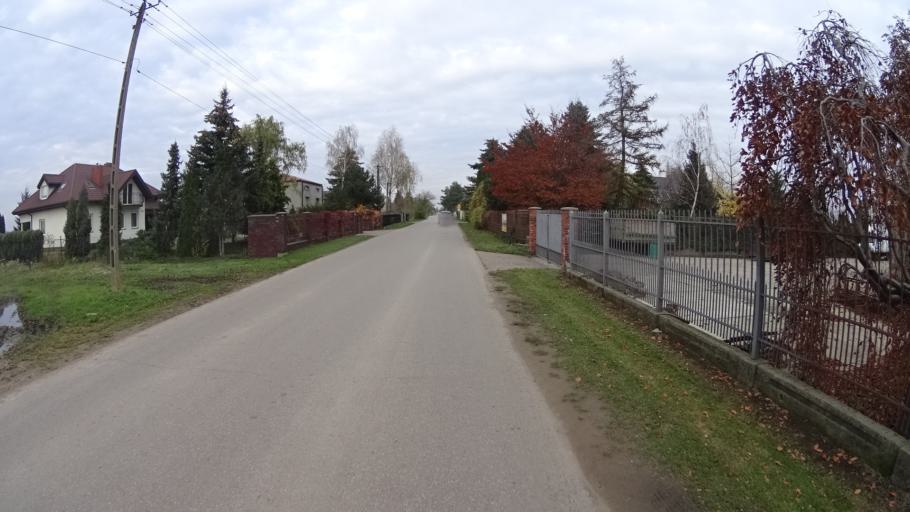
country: PL
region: Masovian Voivodeship
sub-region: Powiat warszawski zachodni
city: Stare Babice
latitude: 52.2386
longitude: 20.8283
